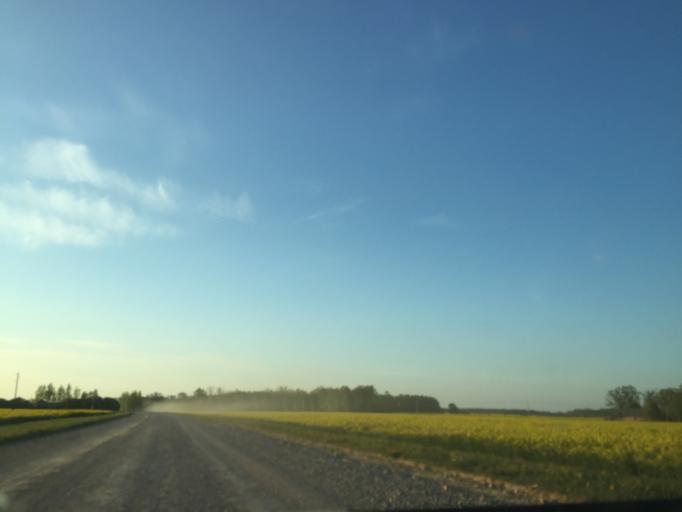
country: LV
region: Bauskas Rajons
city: Bauska
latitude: 56.3423
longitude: 24.1918
